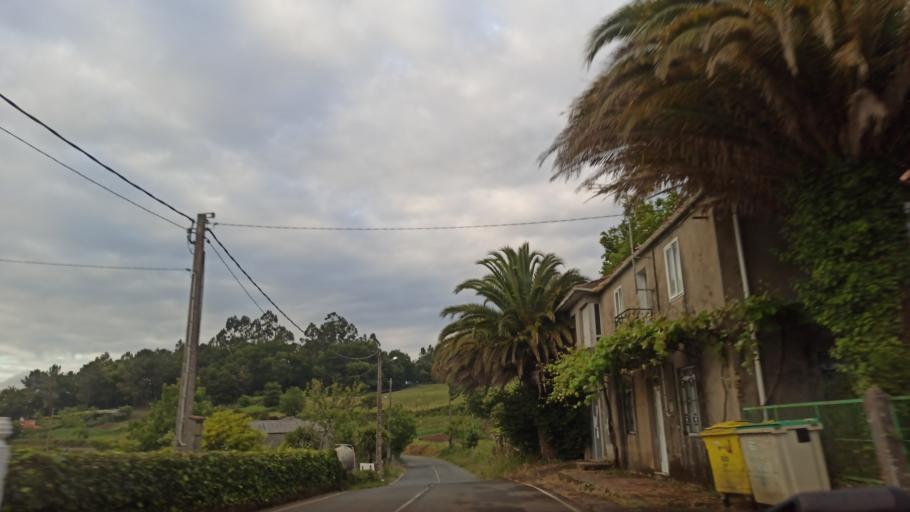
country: ES
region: Galicia
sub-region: Provincia da Coruna
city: Santiso
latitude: 42.8309
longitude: -8.1253
